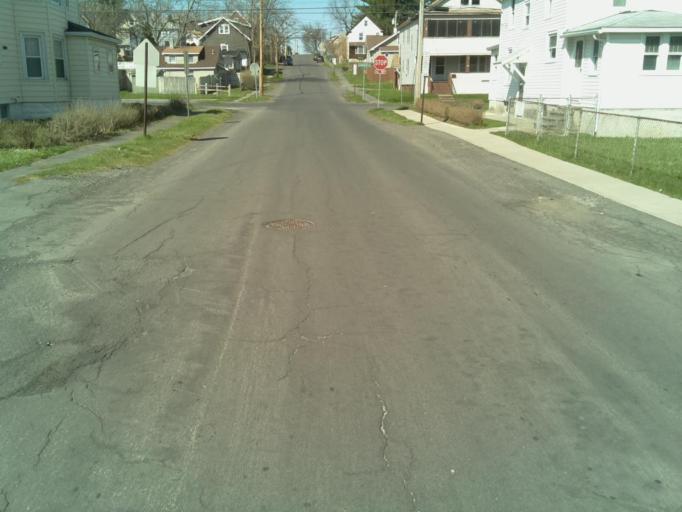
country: US
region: New York
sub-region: Onondaga County
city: Lyncourt
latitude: 43.0708
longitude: -76.1059
